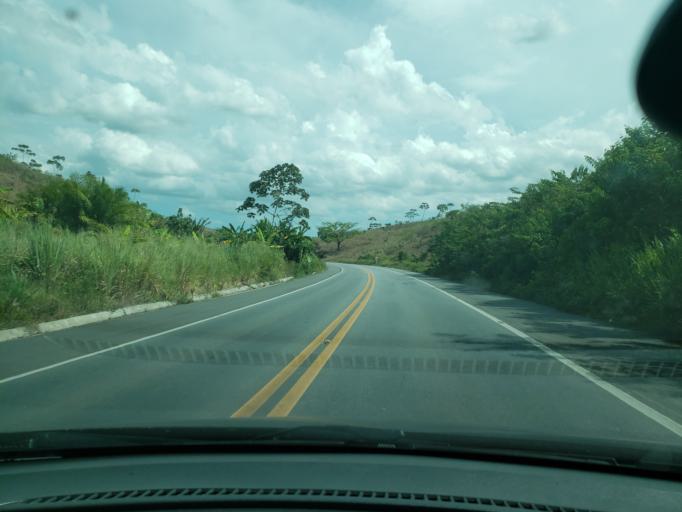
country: BR
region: Alagoas
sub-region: Murici
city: Murici
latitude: -9.2774
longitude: -35.9655
